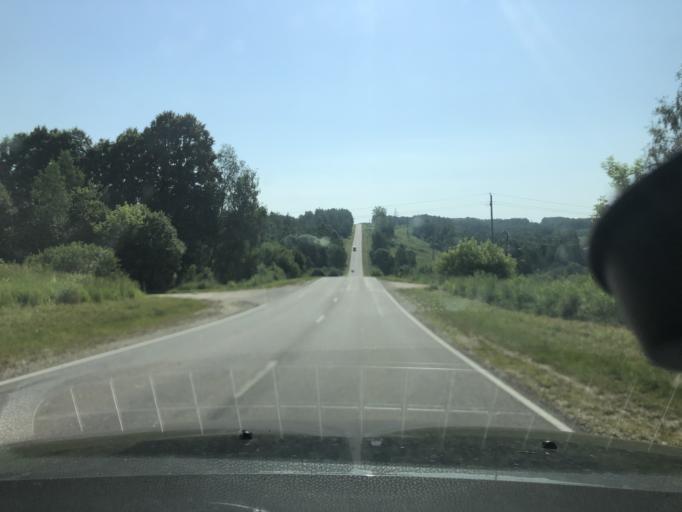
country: RU
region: Tula
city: Dubna
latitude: 54.1457
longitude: 36.9838
